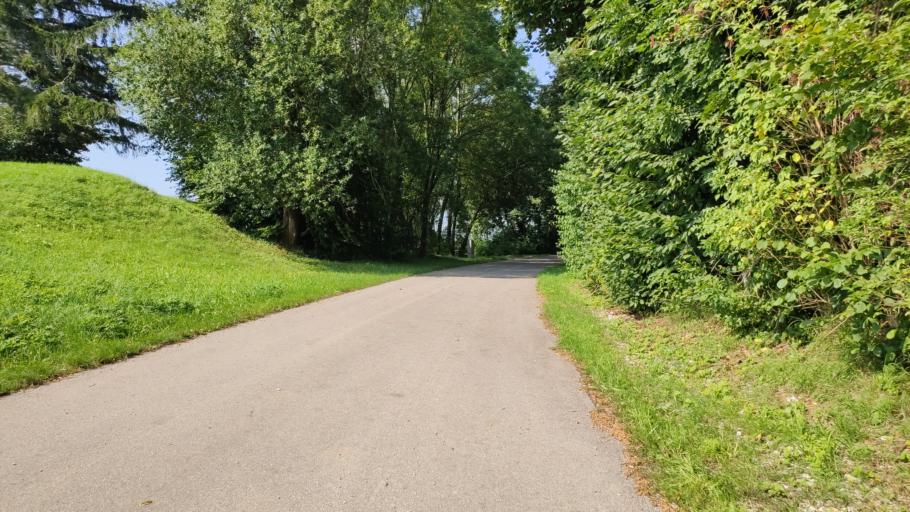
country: DE
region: Bavaria
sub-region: Swabia
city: Graben
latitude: 48.1868
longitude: 10.8159
